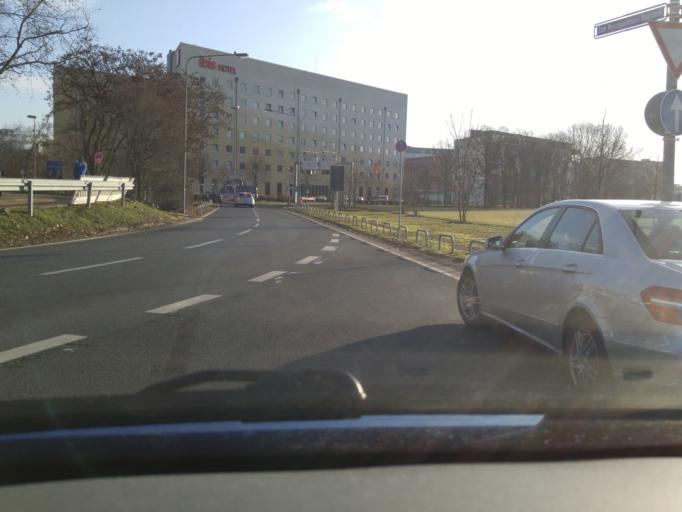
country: DE
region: Hesse
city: Niederrad
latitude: 50.1142
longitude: 8.6164
